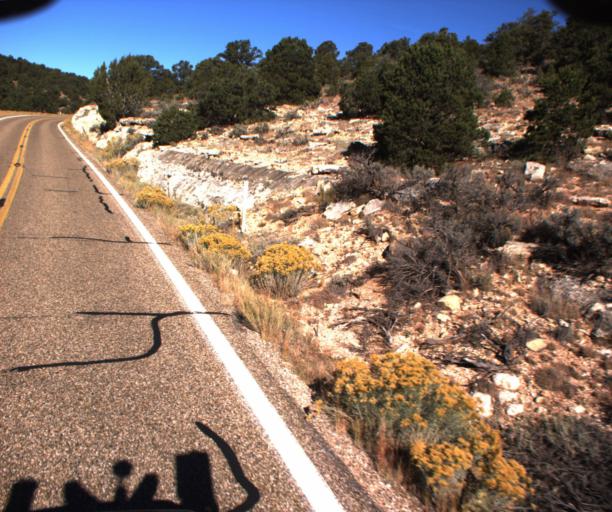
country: US
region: Arizona
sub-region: Coconino County
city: Fredonia
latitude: 36.7315
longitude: -112.0948
